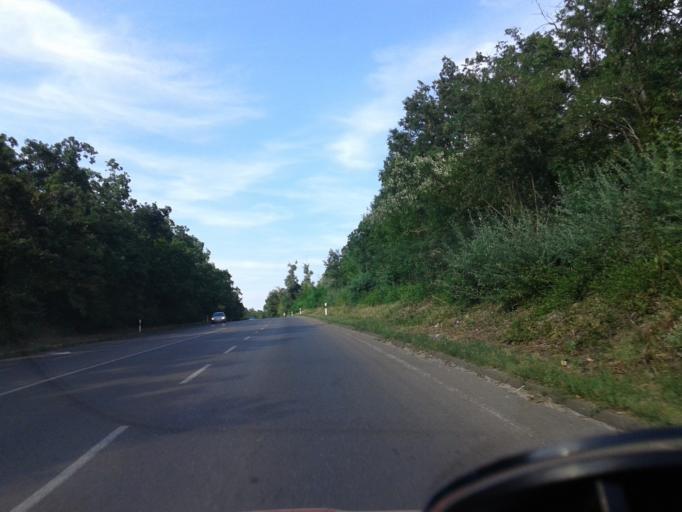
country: HU
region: Pest
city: Kerepes
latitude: 47.5809
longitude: 19.2924
